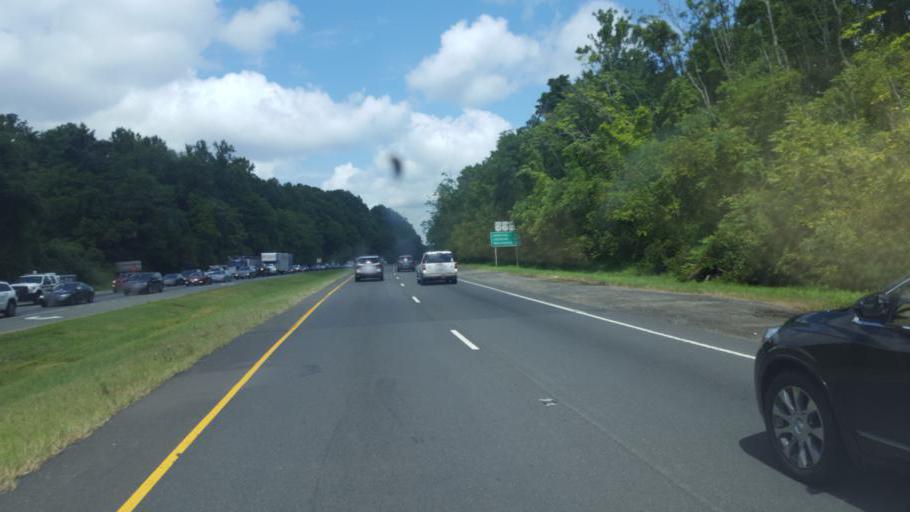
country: US
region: Virginia
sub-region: Fauquier County
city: Warrenton
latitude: 38.6868
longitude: -77.7870
